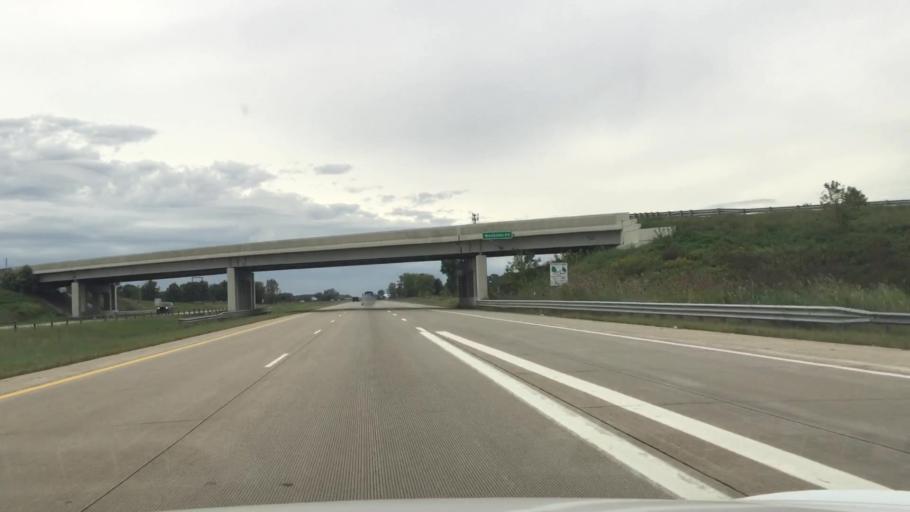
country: US
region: Michigan
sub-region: Saint Clair County
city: Saint Clair
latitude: 42.8630
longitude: -82.5581
